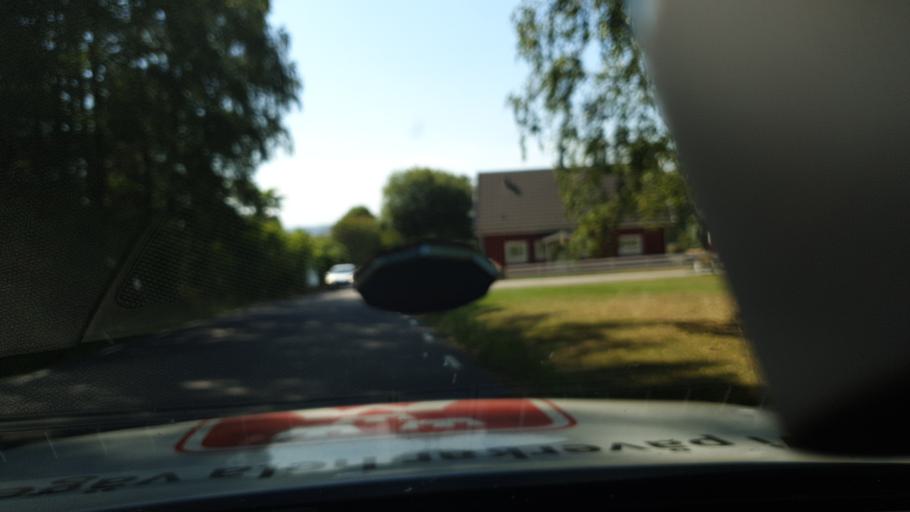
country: SE
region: Skane
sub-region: Sjobo Kommun
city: Blentarp
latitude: 55.5407
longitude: 13.5559
